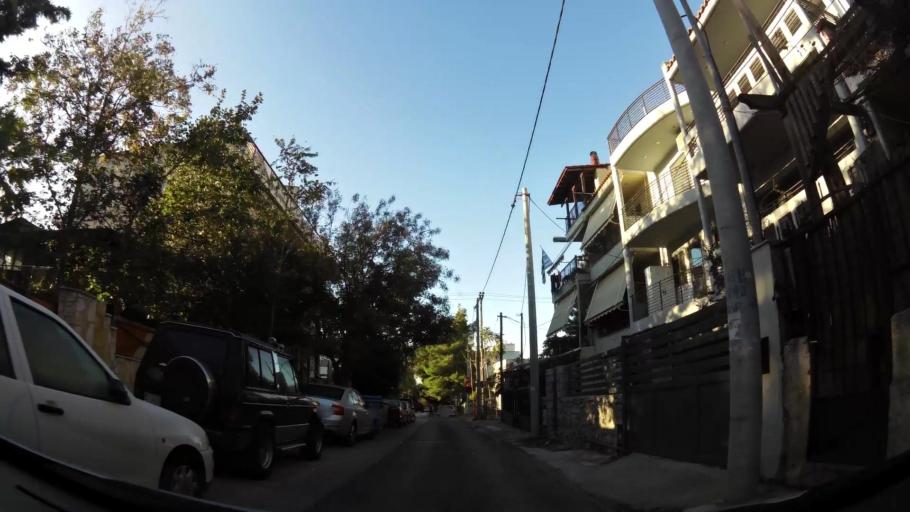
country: GR
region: Attica
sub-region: Nomarchia Athinas
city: Marousi
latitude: 38.0494
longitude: 23.8011
